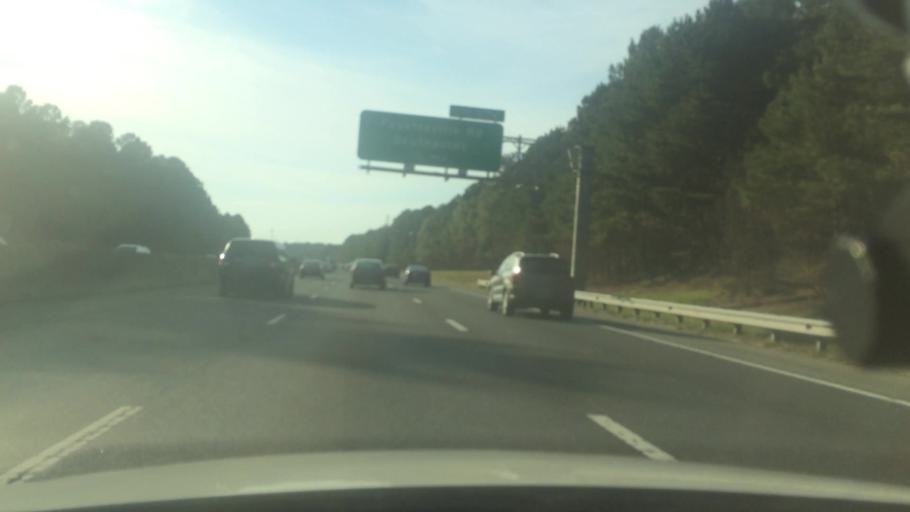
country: US
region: North Carolina
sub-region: Durham County
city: Durham
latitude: 35.9095
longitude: -78.9221
